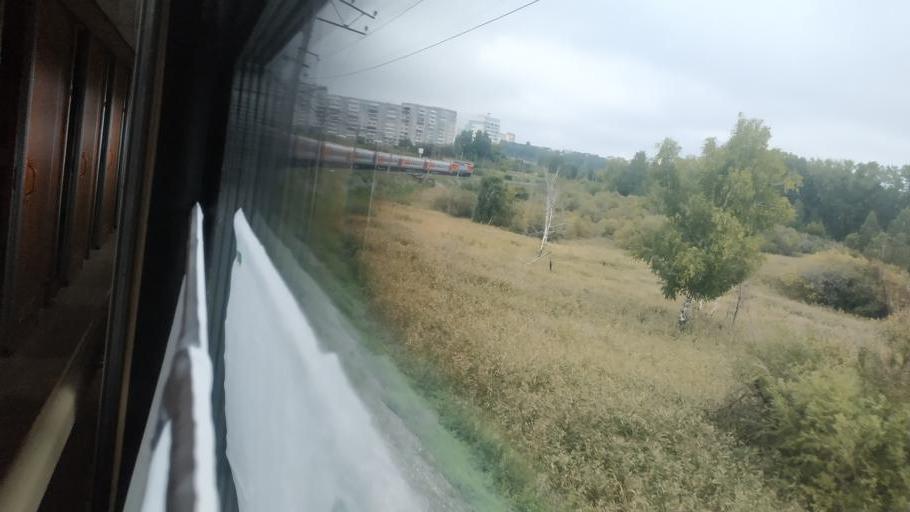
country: RU
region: Tomsk
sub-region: Tomskiy Rayon
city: Tomsk
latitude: 56.4995
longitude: 85.0257
